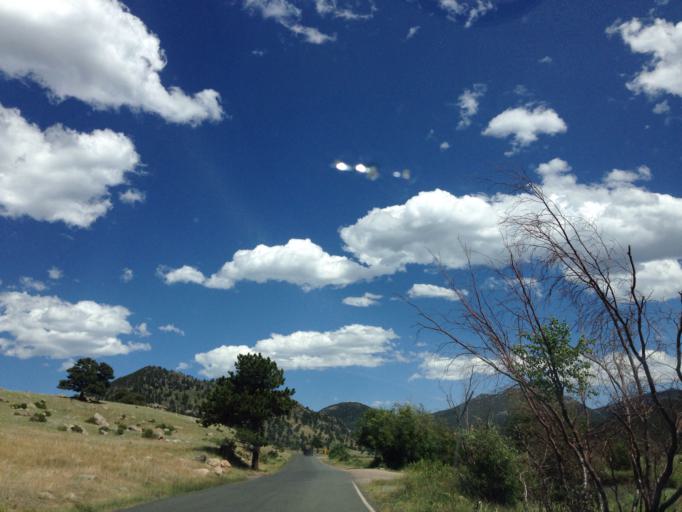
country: US
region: Colorado
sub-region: Larimer County
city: Estes Park
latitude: 40.3568
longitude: -105.6008
